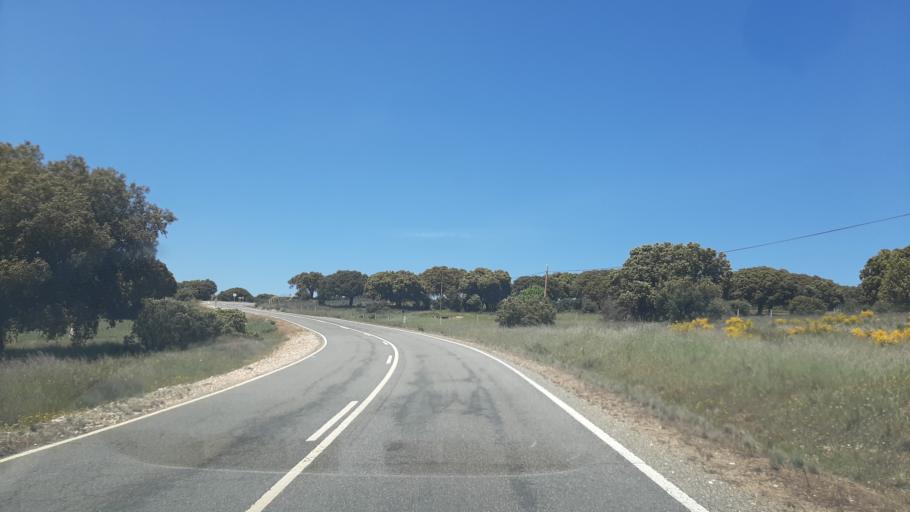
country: ES
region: Castille and Leon
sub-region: Provincia de Salamanca
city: Puente del Congosto
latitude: 40.5295
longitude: -5.5199
